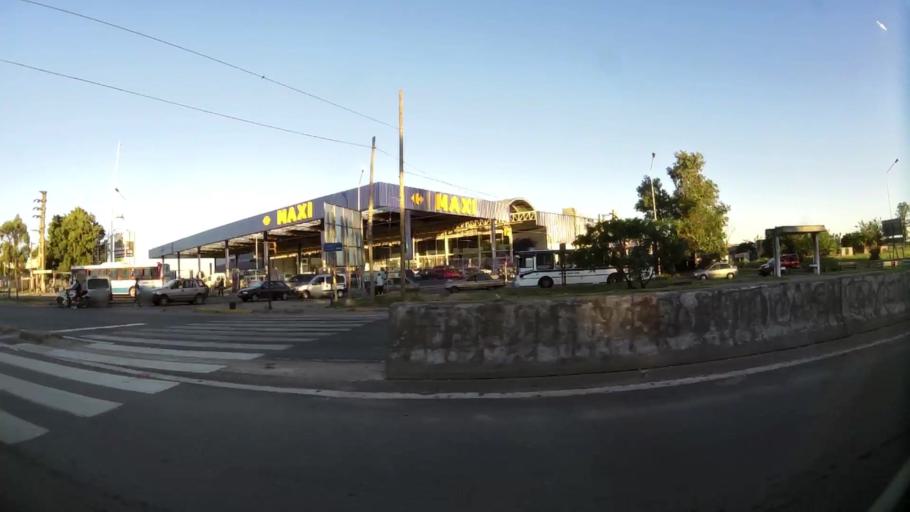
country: AR
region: Buenos Aires
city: Pontevedra
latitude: -34.7549
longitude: -58.6144
